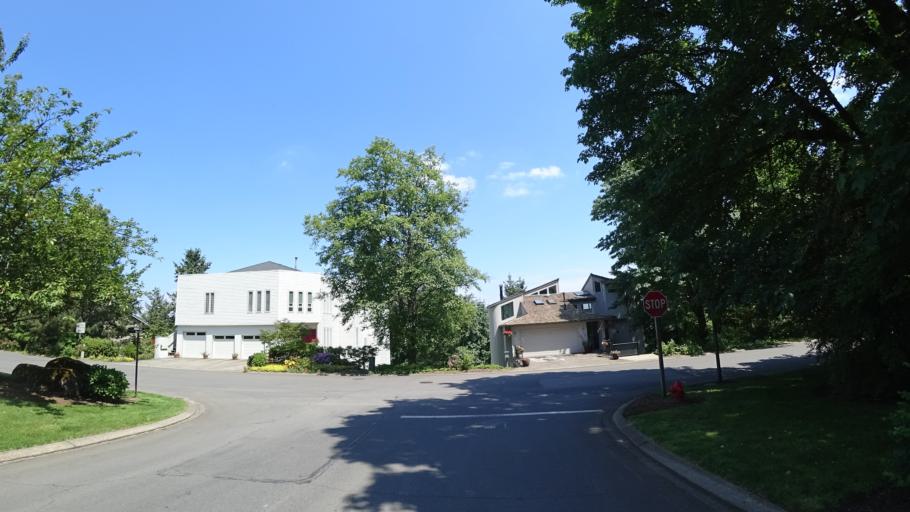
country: US
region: Oregon
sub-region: Washington County
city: Metzger
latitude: 45.4368
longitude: -122.7190
